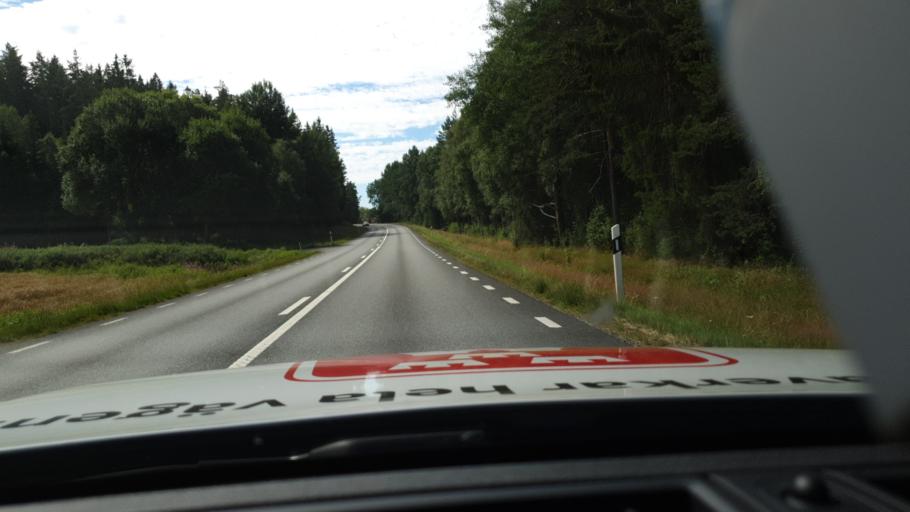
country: SE
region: Joenkoeping
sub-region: Vaggeryds Kommun
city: Vaggeryd
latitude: 57.4637
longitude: 14.3159
